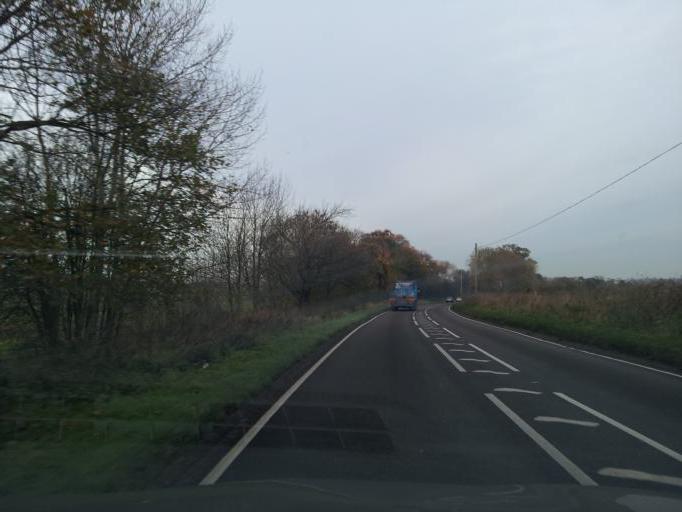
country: GB
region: England
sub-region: Buckinghamshire
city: Stewkley
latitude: 51.8720
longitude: -0.7539
